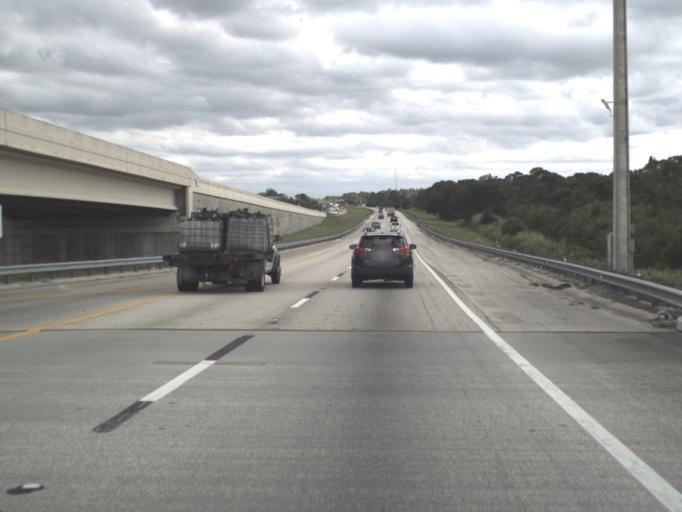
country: US
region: Florida
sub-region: Martin County
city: Palm City
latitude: 27.1145
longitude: -80.2729
